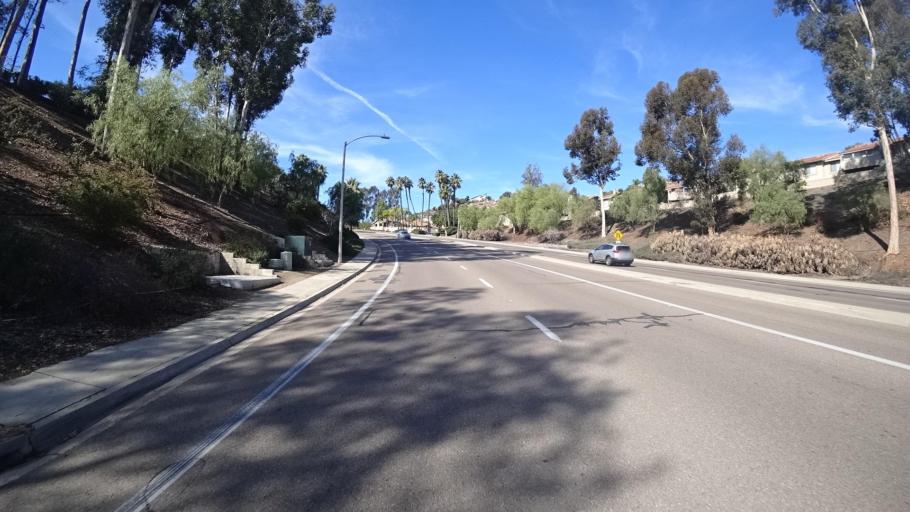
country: US
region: California
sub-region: San Diego County
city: Rancho San Diego
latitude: 32.7514
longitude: -116.9428
